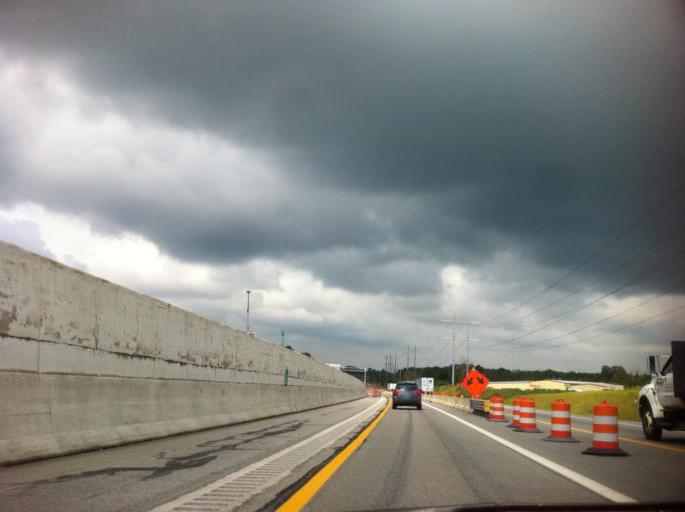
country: US
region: Ohio
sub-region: Cuyahoga County
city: North Royalton
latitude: 41.3146
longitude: -81.7605
